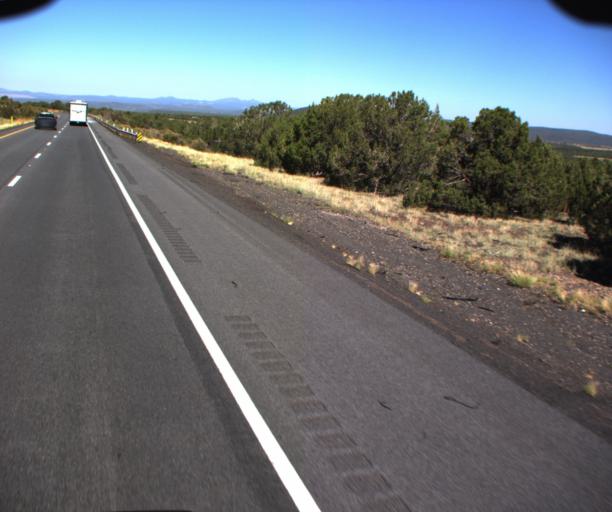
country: US
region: Arizona
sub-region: Coconino County
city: Williams
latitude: 35.2163
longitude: -112.3660
